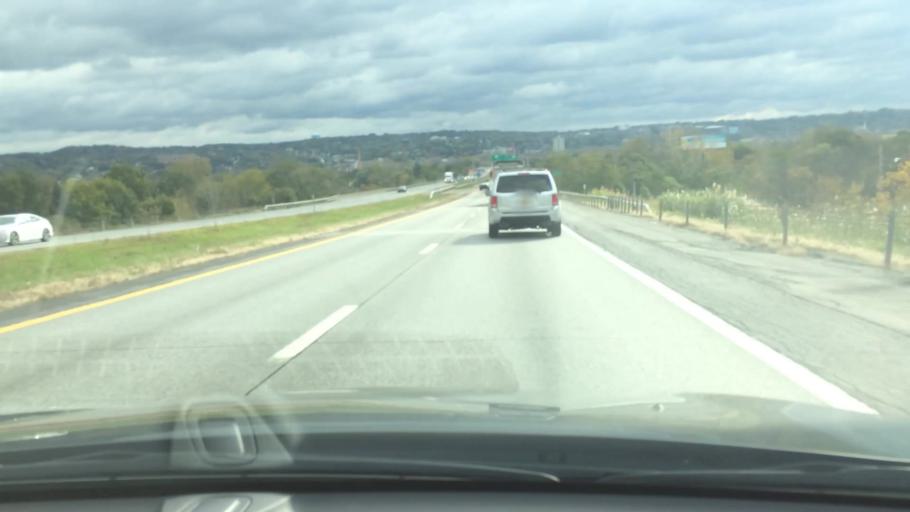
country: US
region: New York
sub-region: Albany County
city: Green Island
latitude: 42.7473
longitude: -73.7086
